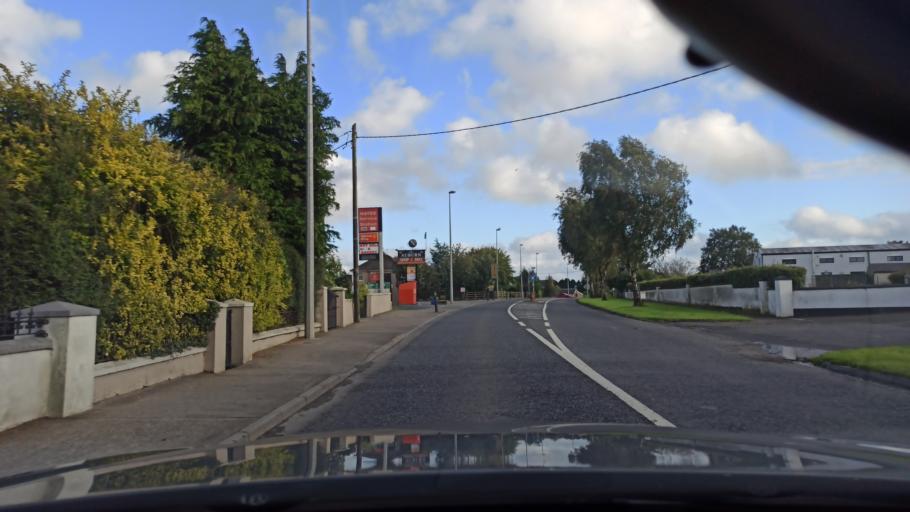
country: IE
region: Munster
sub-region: North Tipperary
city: Roscrea
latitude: 52.9405
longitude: -7.7885
